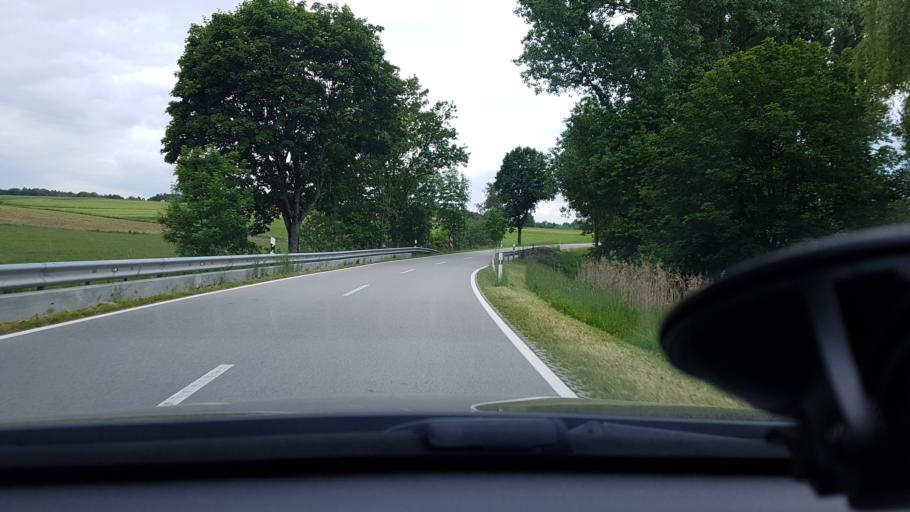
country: DE
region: Bavaria
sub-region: Lower Bavaria
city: Wittibreut
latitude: 48.3496
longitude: 13.0182
